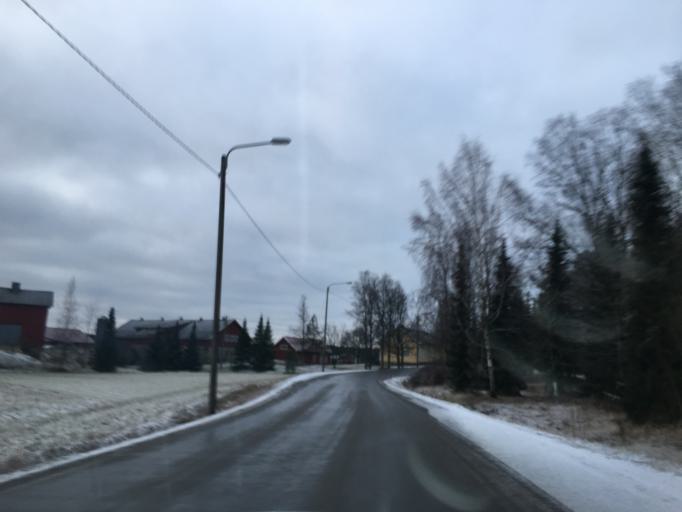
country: FI
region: Varsinais-Suomi
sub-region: Loimaa
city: Aura
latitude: 60.5949
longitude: 22.5344
